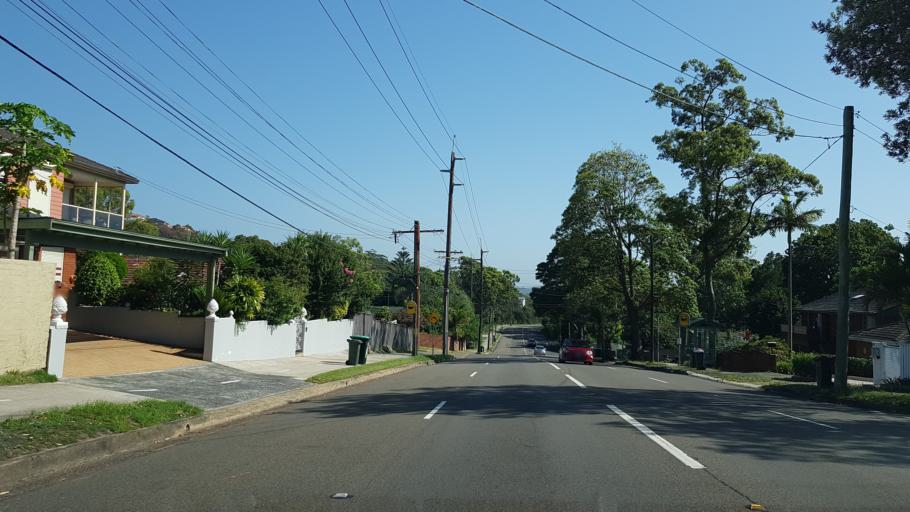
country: AU
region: New South Wales
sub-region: Warringah
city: Narraweena
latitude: -33.7506
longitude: 151.2616
